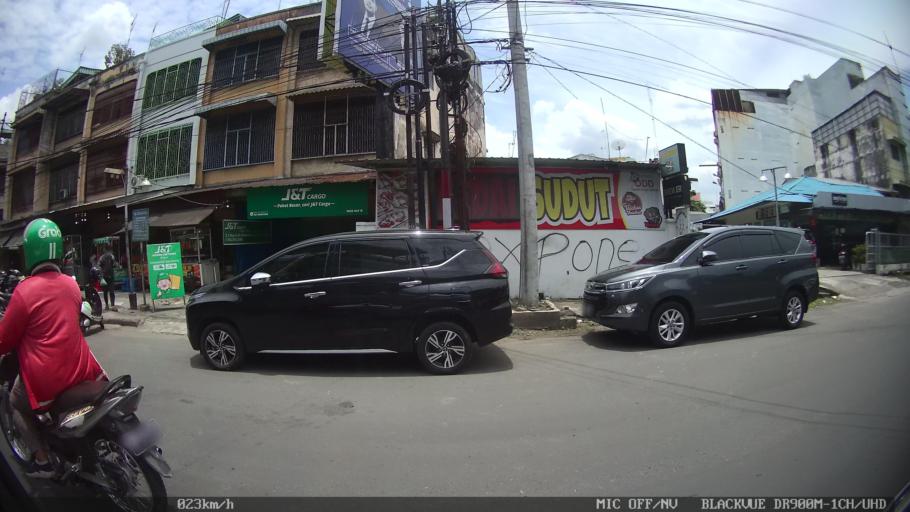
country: ID
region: North Sumatra
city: Medan
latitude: 3.5917
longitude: 98.6690
